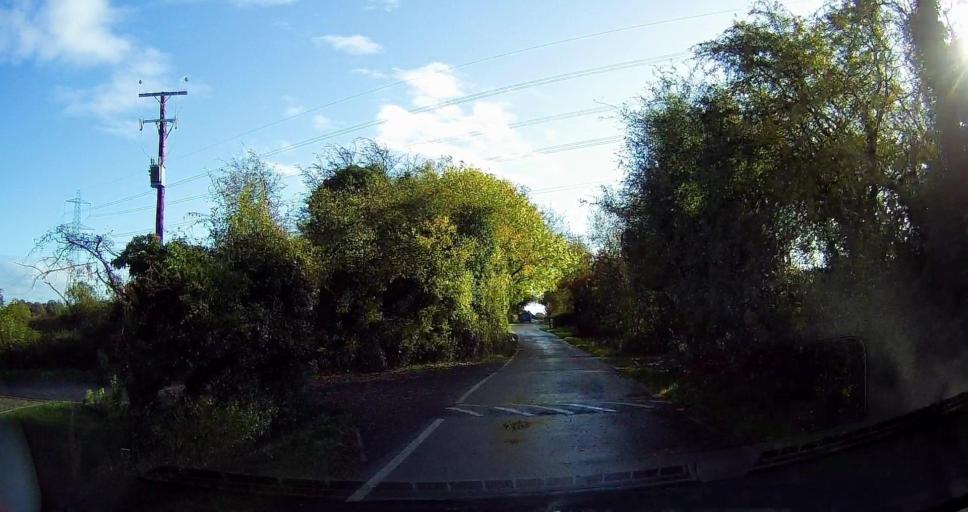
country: GB
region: England
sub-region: Staffordshire
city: Whittington
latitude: 52.6893
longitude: -1.7746
